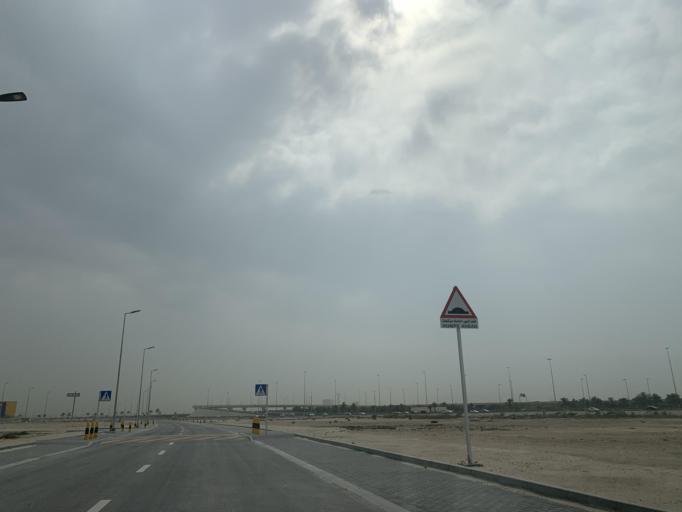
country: BH
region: Northern
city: Madinat `Isa
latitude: 26.1864
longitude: 50.5090
